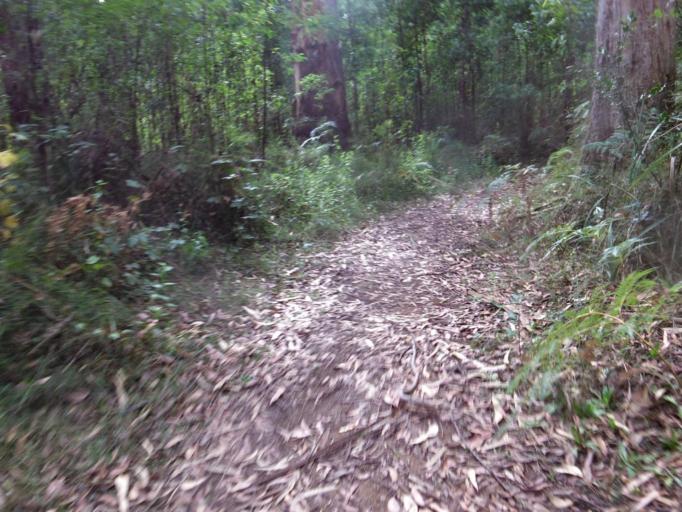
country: AU
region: Victoria
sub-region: Yarra Ranges
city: Healesville
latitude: -37.5409
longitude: 145.4772
